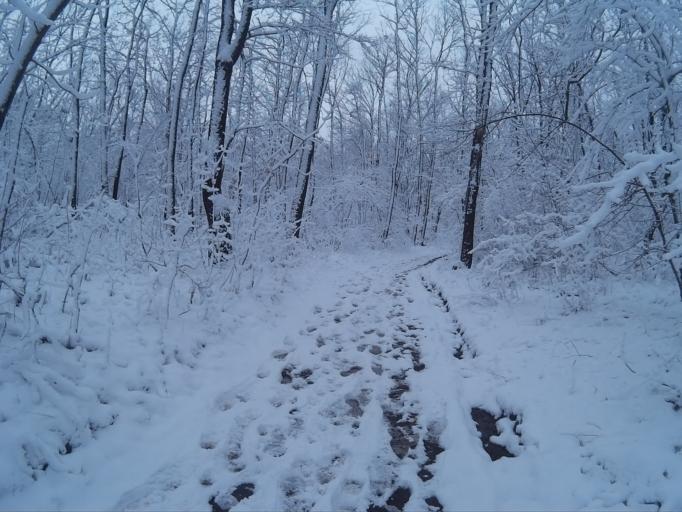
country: HU
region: Fejer
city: Szarliget
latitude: 47.5158
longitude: 18.5082
